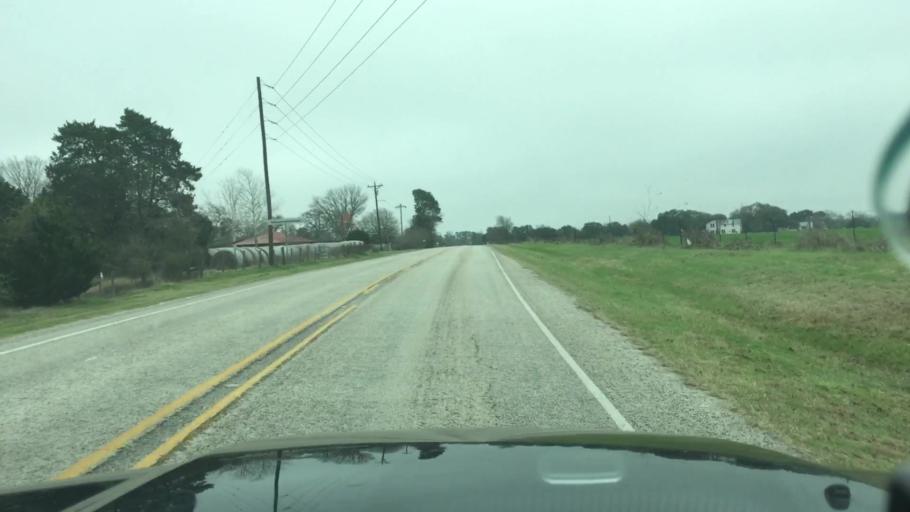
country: US
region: Texas
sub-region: Fayette County
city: La Grange
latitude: 30.0058
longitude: -96.9046
